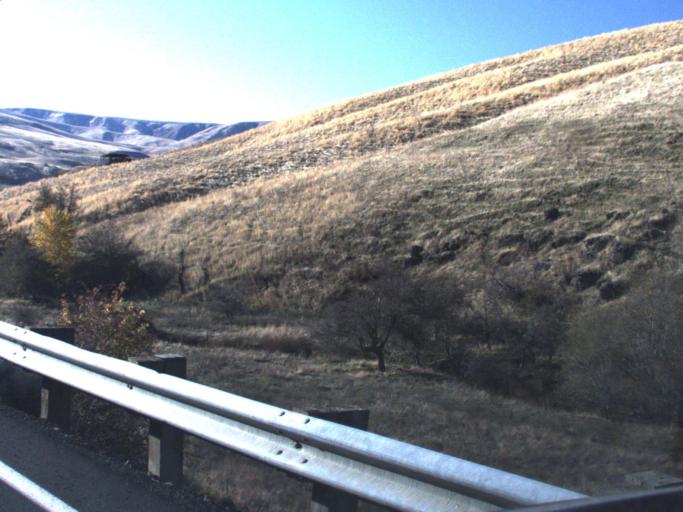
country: US
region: Washington
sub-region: Whitman County
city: Colfax
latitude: 46.7112
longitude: -117.4656
